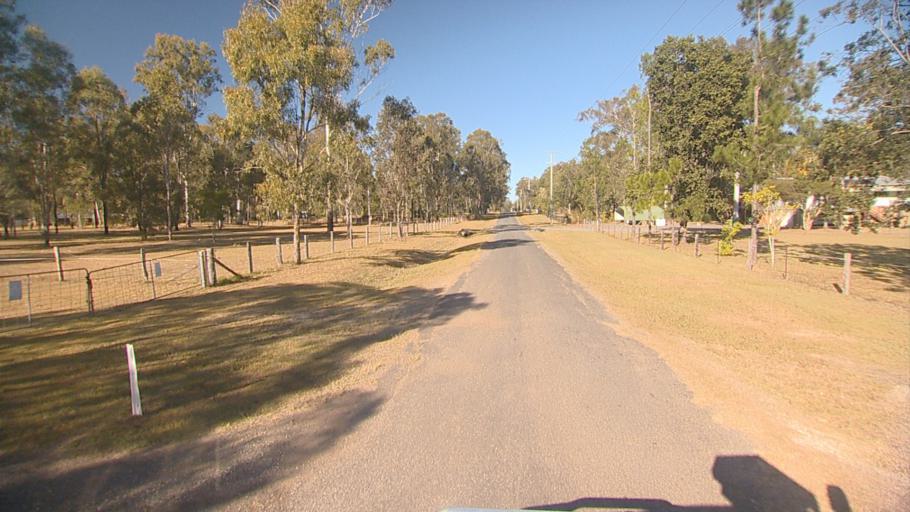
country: AU
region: Queensland
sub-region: Logan
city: Park Ridge South
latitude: -27.7505
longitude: 153.0346
